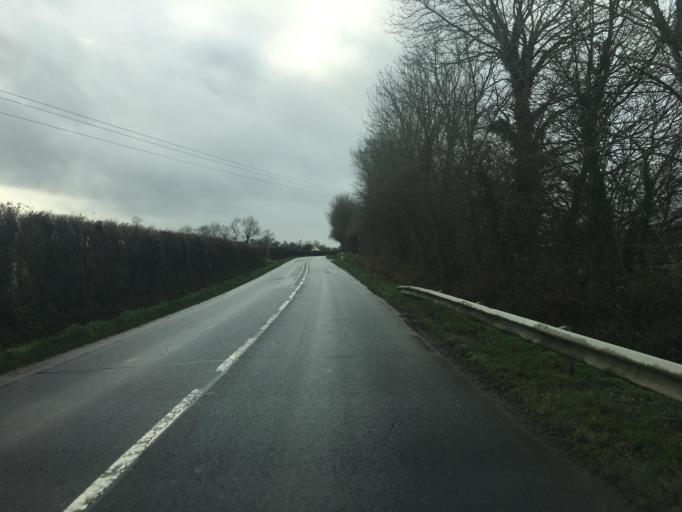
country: FR
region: Lower Normandy
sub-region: Departement du Calvados
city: Isigny-sur-Mer
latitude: 49.3531
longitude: -1.0752
